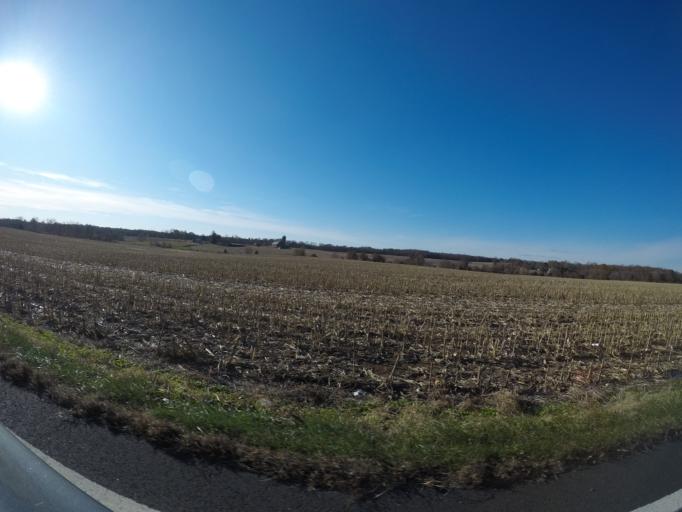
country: US
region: Maryland
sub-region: Harford County
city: Riverside
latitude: 39.5145
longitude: -76.2670
